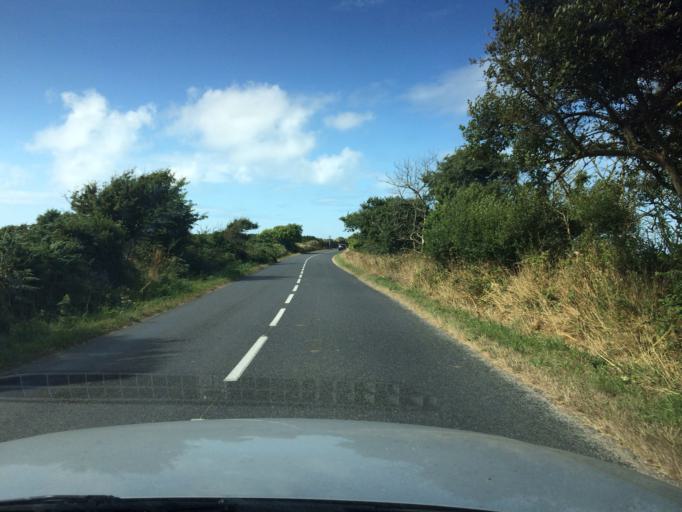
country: FR
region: Lower Normandy
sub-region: Departement de la Manche
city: Beaumont-Hague
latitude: 49.7052
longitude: -1.9307
